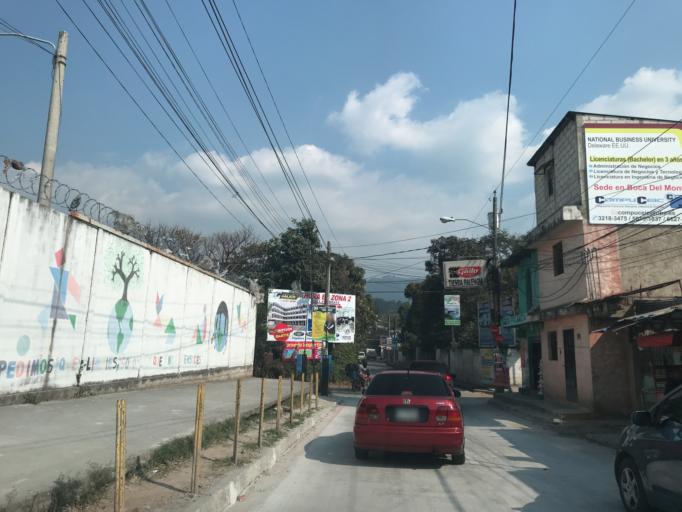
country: GT
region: Guatemala
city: Santa Catarina Pinula
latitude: 14.5500
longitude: -90.5253
